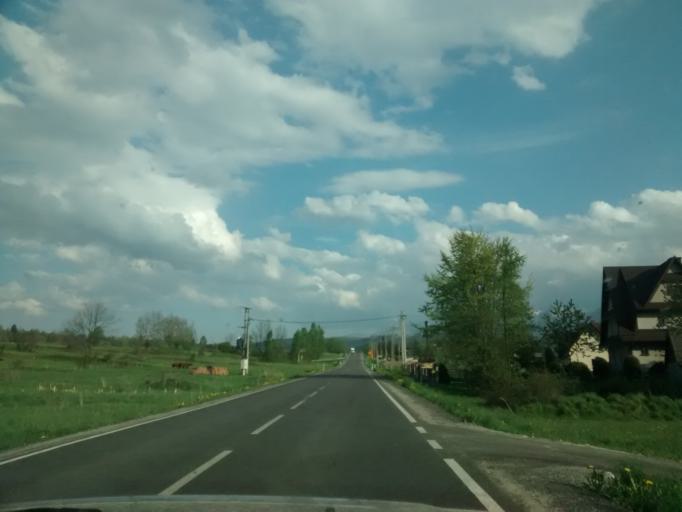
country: PL
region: Lesser Poland Voivodeship
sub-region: Powiat tatrzanski
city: Bukowina Tatrzanska
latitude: 49.3441
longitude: 20.1383
